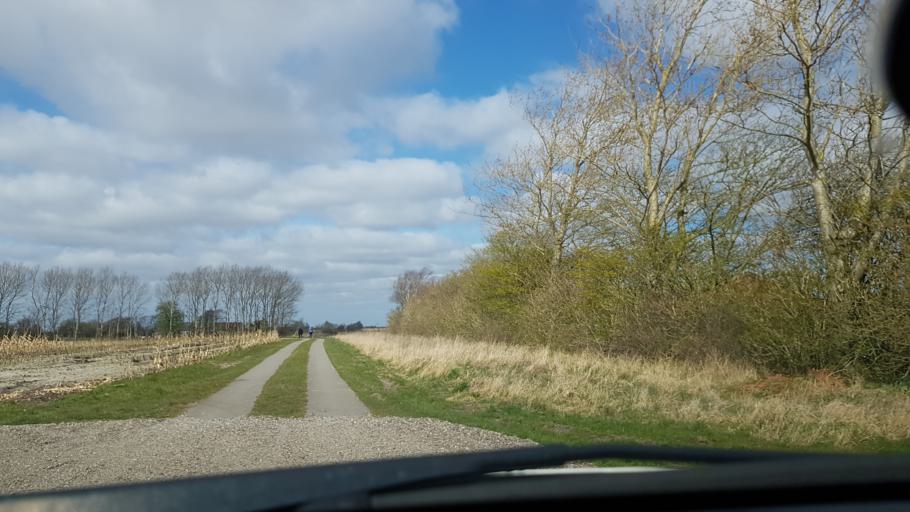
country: DK
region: South Denmark
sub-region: Esbjerg Kommune
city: Ribe
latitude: 55.2536
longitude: 8.8388
